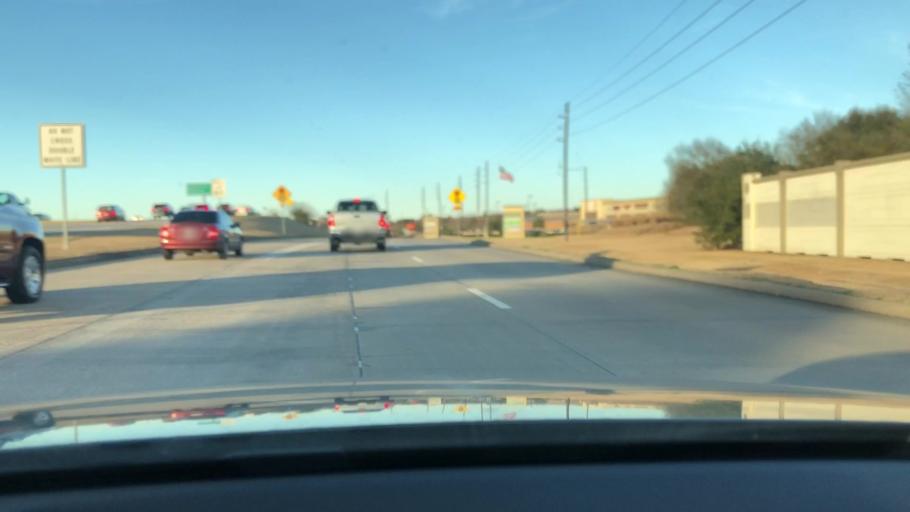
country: US
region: Texas
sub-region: Fort Bend County
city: Cinco Ranch
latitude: 29.7113
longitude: -95.7742
